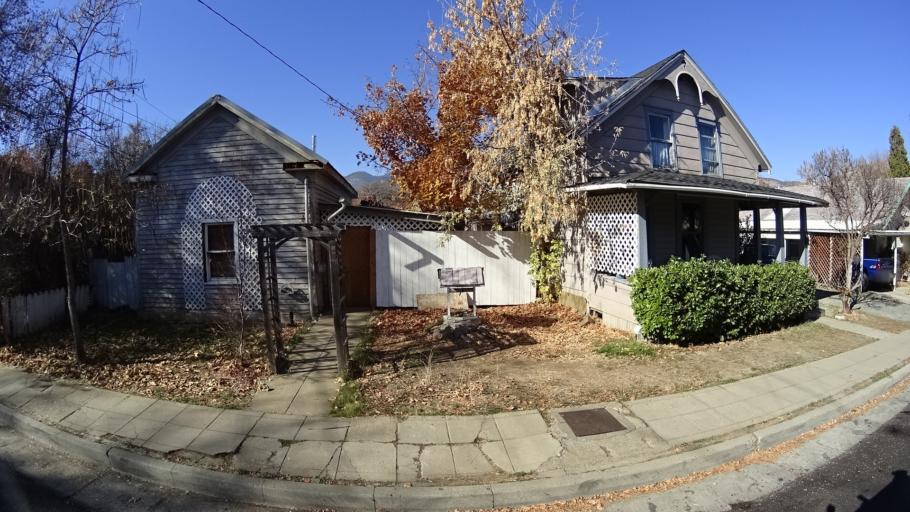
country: US
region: California
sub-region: Siskiyou County
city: Yreka
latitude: 41.7306
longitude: -122.6416
